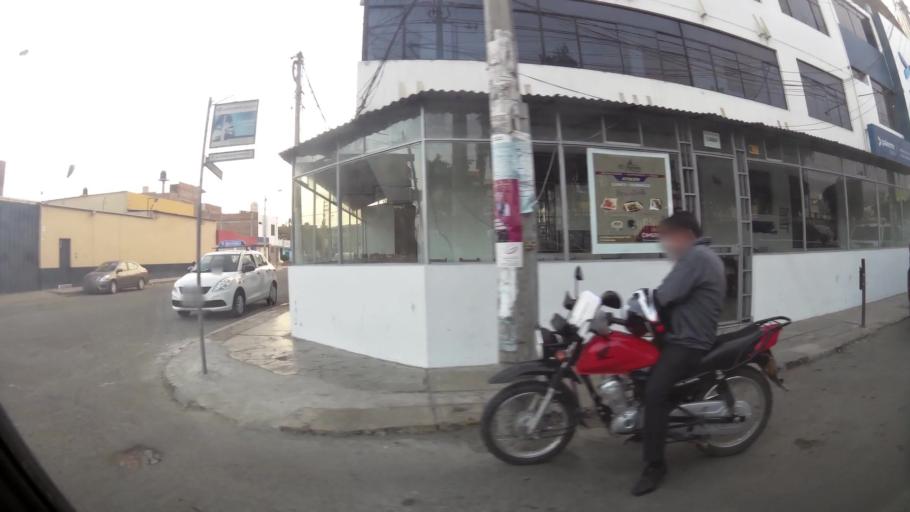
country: PE
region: La Libertad
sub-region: Provincia de Trujillo
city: Trujillo
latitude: -8.0992
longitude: -79.0374
